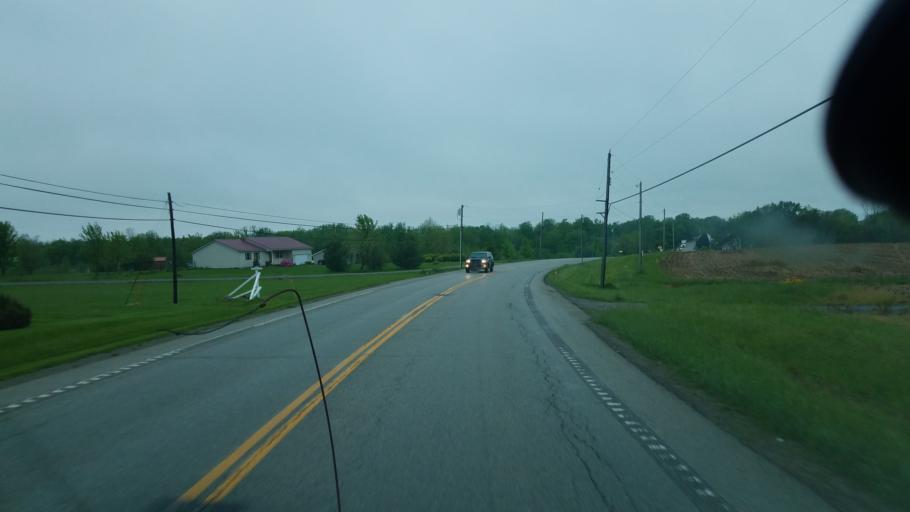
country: US
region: Ohio
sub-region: Highland County
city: Leesburg
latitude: 39.2796
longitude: -83.5941
